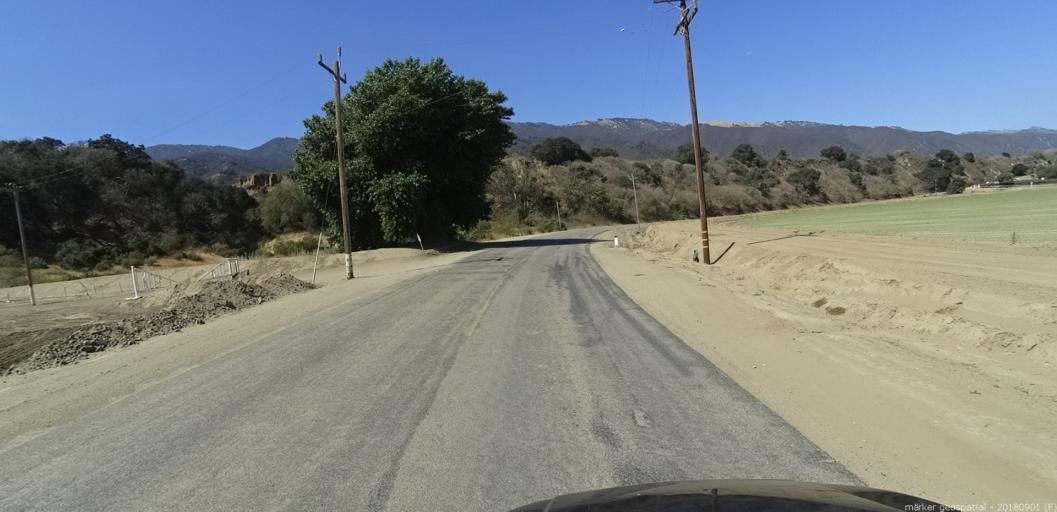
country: US
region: California
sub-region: Monterey County
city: Gonzales
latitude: 36.4781
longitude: -121.4797
